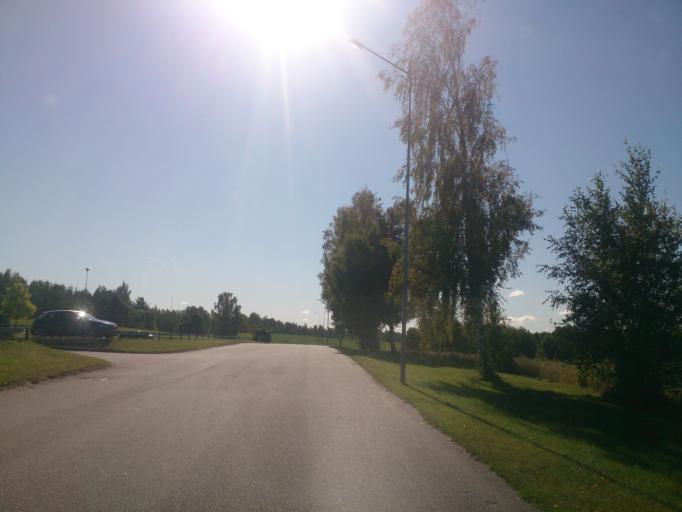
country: SE
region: OEstergoetland
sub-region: Atvidabergs Kommun
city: Atvidaberg
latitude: 58.2275
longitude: 15.9705
